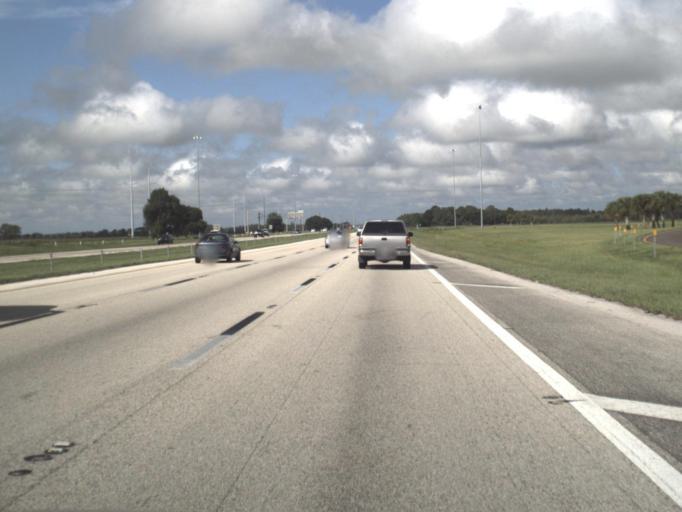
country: US
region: Florida
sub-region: Polk County
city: Polk City
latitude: 28.1539
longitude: -81.8490
